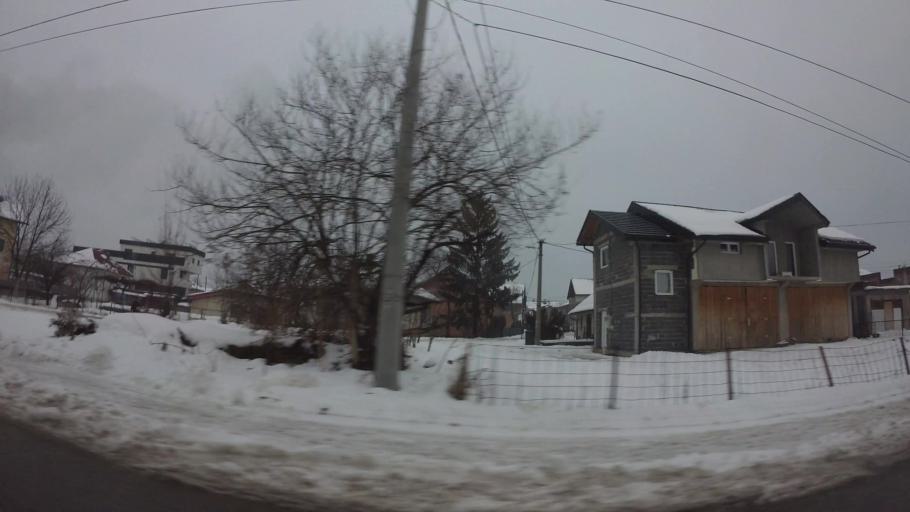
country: BA
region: Federation of Bosnia and Herzegovina
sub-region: Kanton Sarajevo
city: Sarajevo
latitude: 43.8496
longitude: 18.3065
